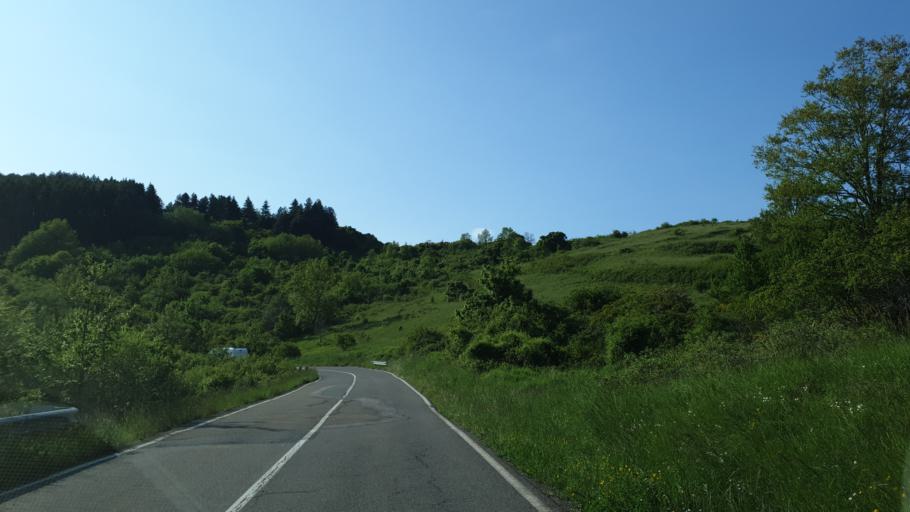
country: IT
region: Tuscany
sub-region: Province of Arezzo
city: Stia
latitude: 43.7818
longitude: 11.6572
